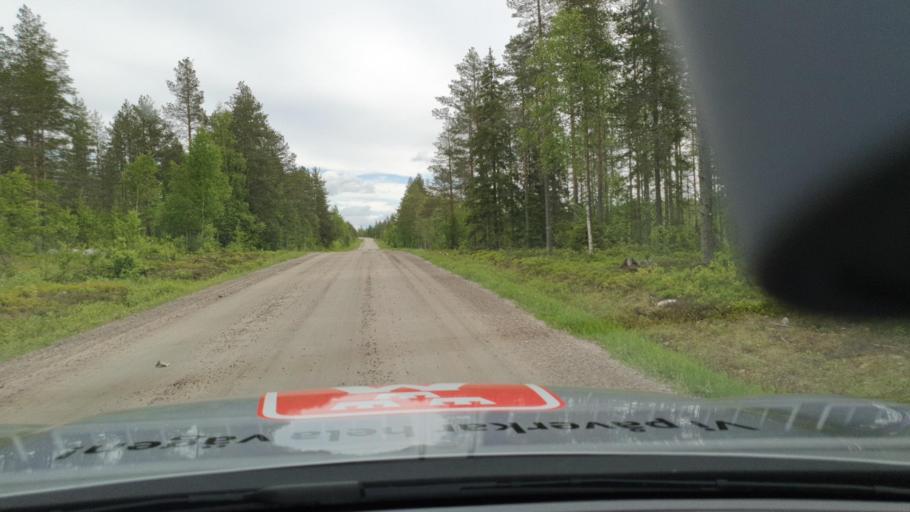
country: SE
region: Norrbotten
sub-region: Kalix Kommun
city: Kalix
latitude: 65.9275
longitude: 23.5095
